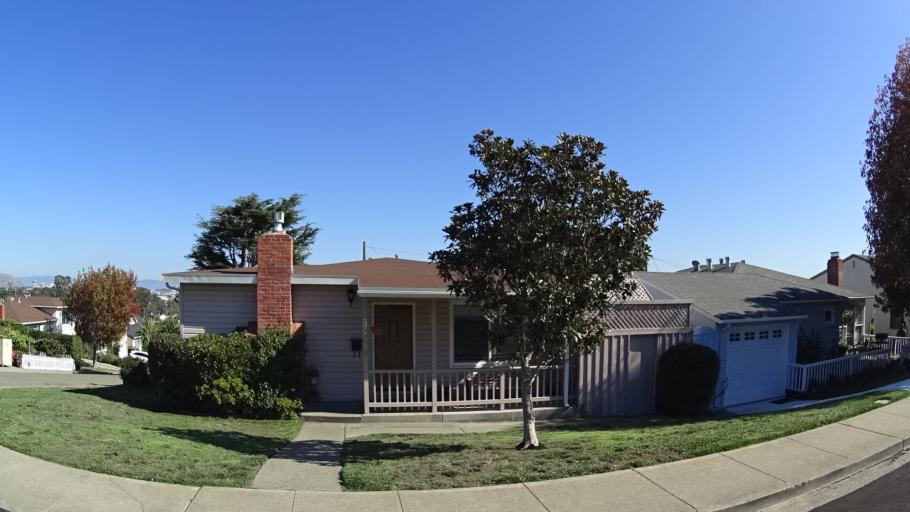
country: US
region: California
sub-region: San Mateo County
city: San Bruno
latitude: 37.6235
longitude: -122.4258
